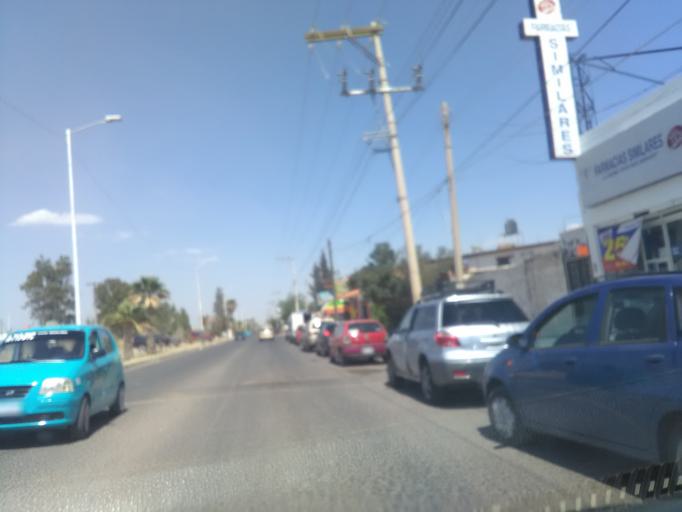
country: MX
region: Durango
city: Victoria de Durango
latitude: 24.0439
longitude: -104.6461
